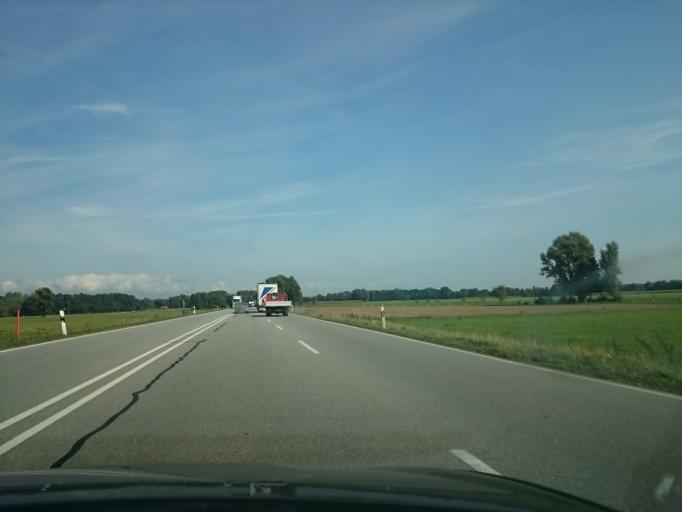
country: DE
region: Bavaria
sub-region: Upper Bavaria
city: Pornbach
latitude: 48.6265
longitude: 11.4440
